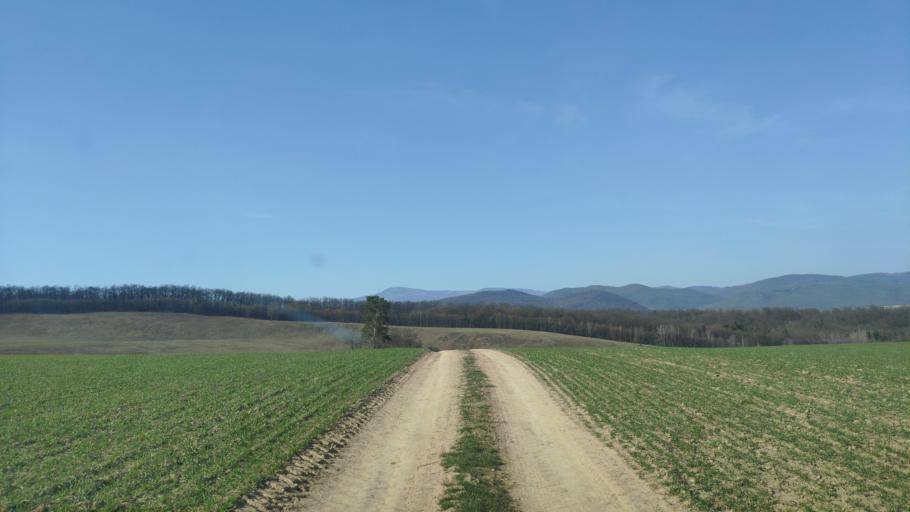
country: SK
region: Banskobystricky
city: Revuca
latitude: 48.5493
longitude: 20.2738
